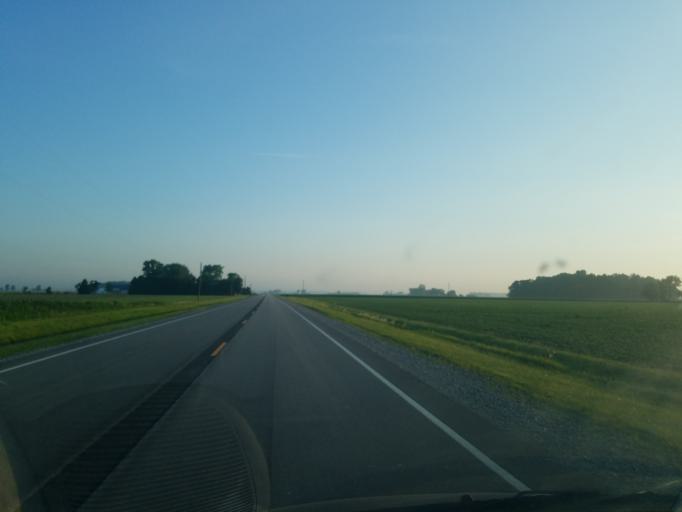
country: US
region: Indiana
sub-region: Allen County
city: Woodburn
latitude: 41.1752
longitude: -84.8492
